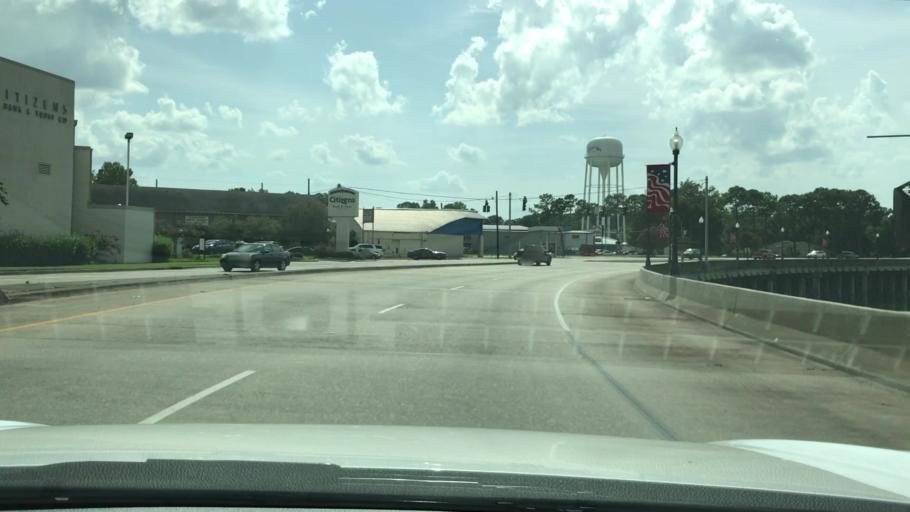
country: US
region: Louisiana
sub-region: Iberville Parish
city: Plaquemine
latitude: 30.2916
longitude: -91.2358
